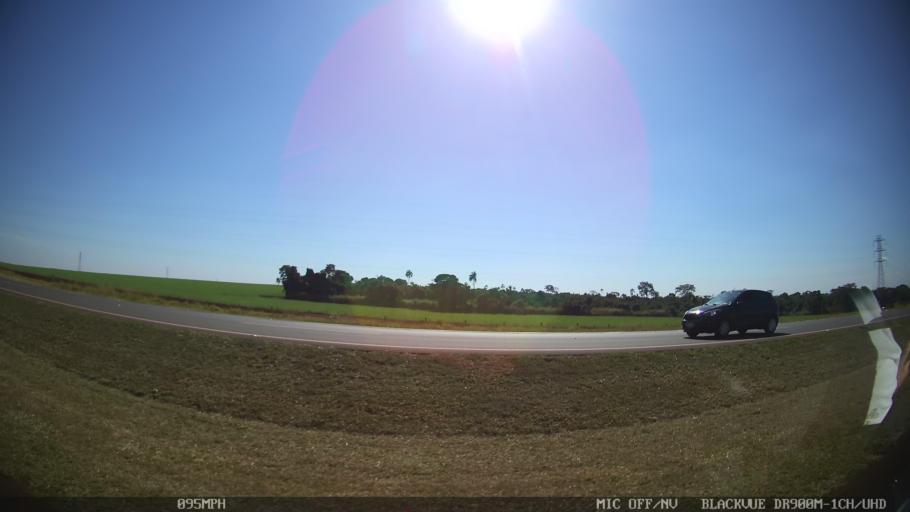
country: BR
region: Sao Paulo
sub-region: Ribeirao Preto
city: Ribeirao Preto
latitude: -21.1508
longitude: -47.8856
